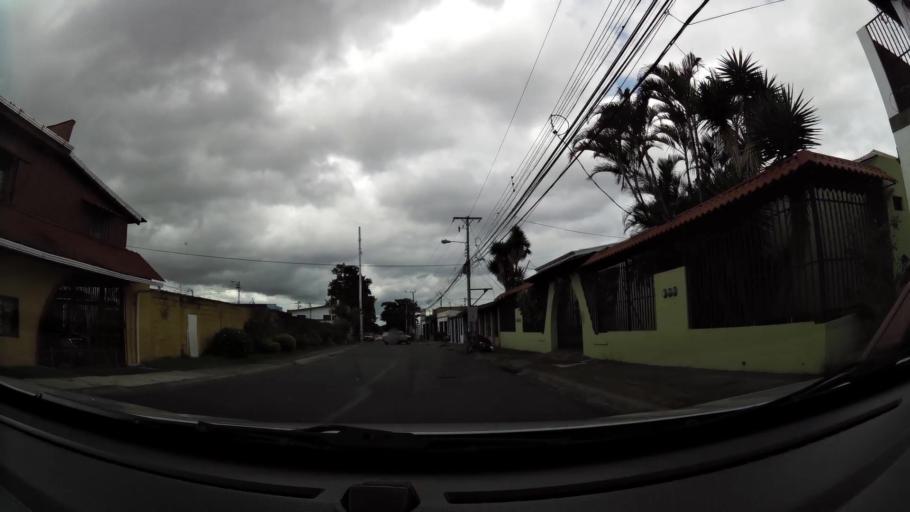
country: CR
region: San Jose
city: San Pedro
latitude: 9.9217
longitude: -84.0422
